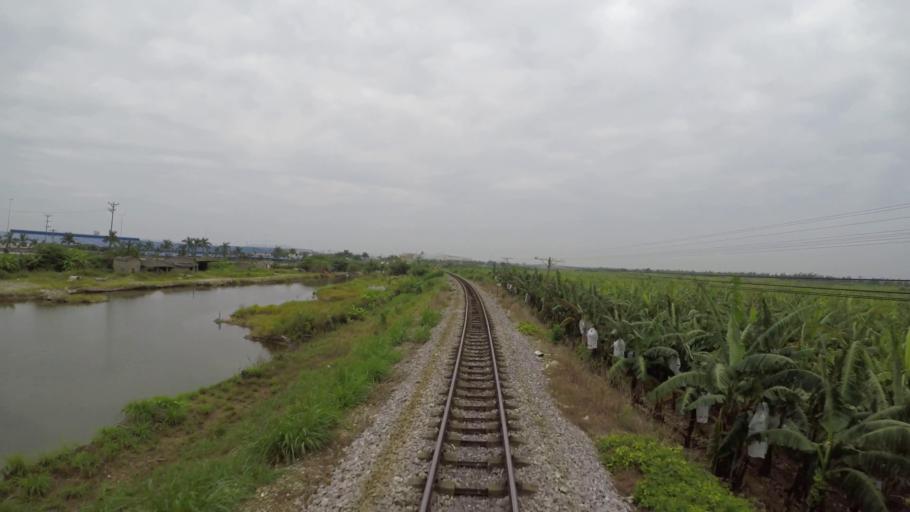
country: VN
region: Hai Duong
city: Nam Sach
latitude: 20.9752
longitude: 106.3942
